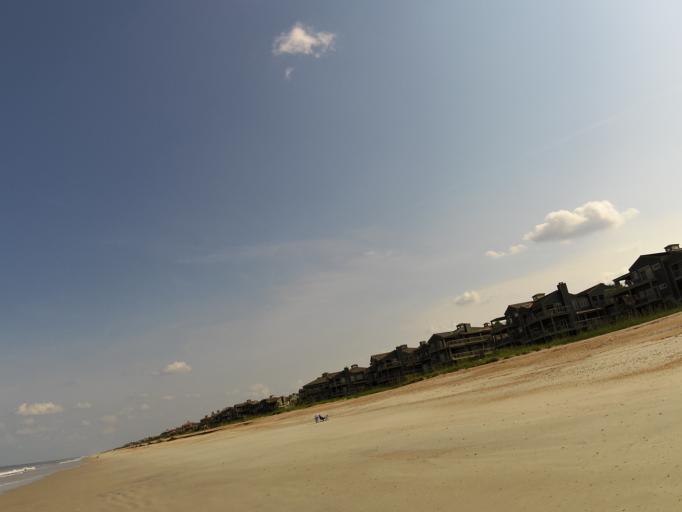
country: US
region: Florida
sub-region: Saint Johns County
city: Palm Valley
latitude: 30.1434
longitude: -81.3507
